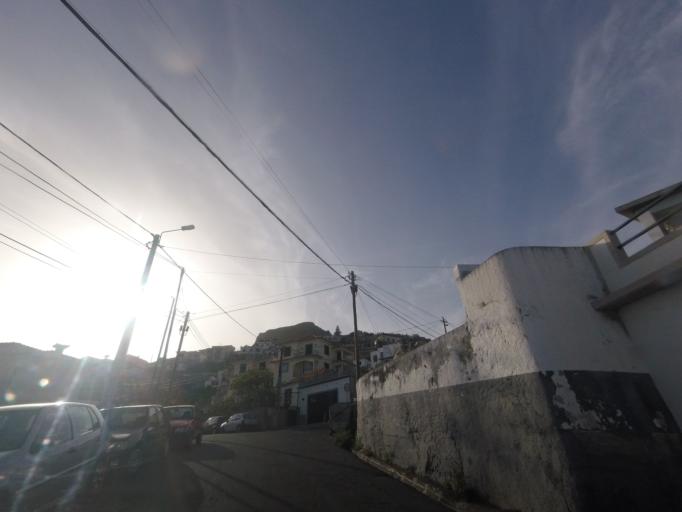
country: PT
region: Madeira
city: Camara de Lobos
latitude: 32.6538
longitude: -16.9875
